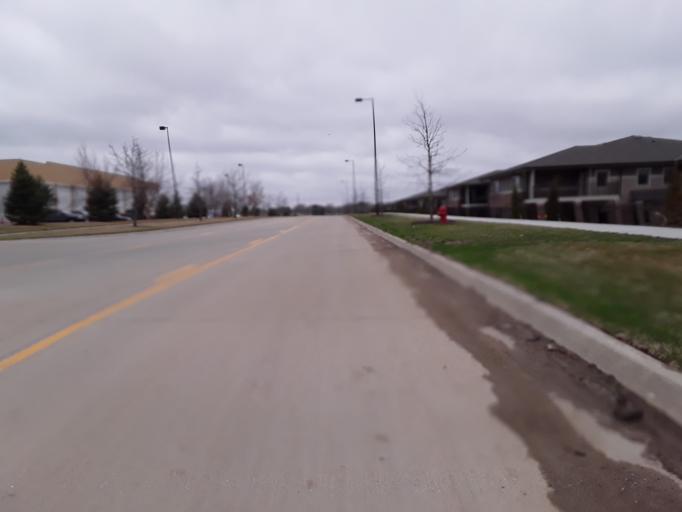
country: US
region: Nebraska
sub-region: Lancaster County
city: Lincoln
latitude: 40.8499
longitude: -96.6009
